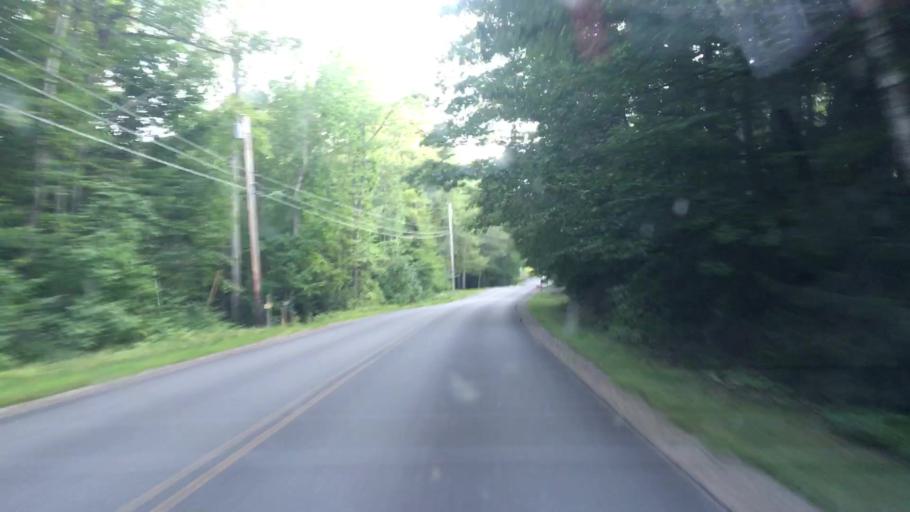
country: US
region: Maine
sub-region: Penobscot County
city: Hampden
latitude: 44.6981
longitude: -68.8959
